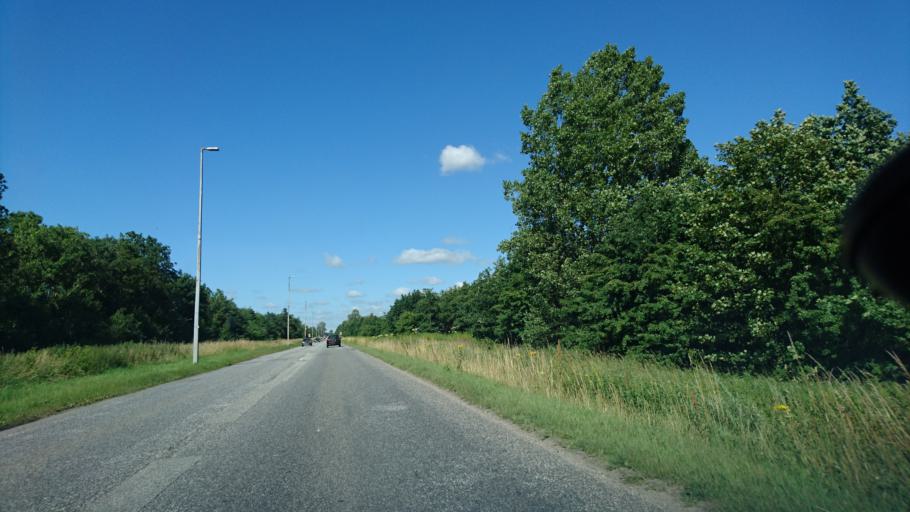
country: DK
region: North Denmark
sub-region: Alborg Kommune
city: Gistrup
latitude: 57.0257
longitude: 10.0082
